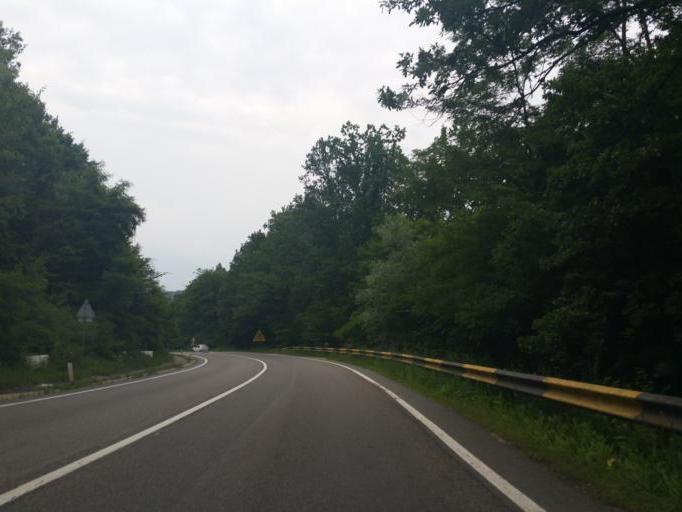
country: RO
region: Salaj
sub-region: Comuna Romanasi
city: Romanasi
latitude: 47.0728
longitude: 23.2041
